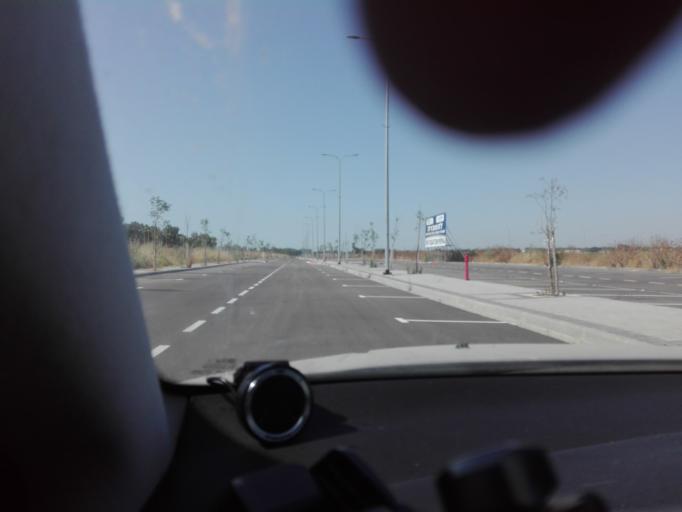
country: IL
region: Central District
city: Bene 'Ayish
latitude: 31.7242
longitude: 34.7557
